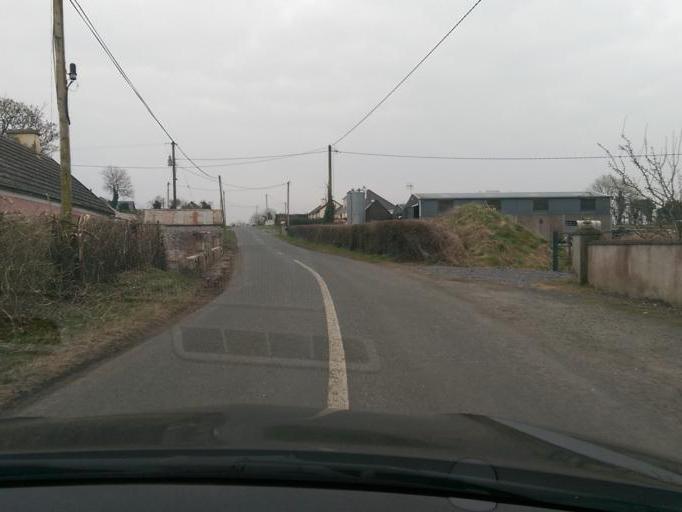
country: IE
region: Leinster
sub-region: An Longfort
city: Longford
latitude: 53.6581
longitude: -7.8352
